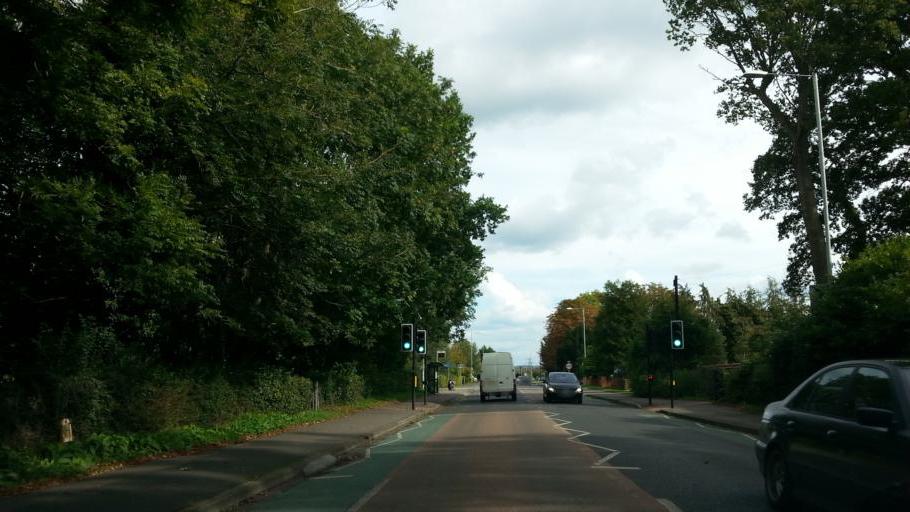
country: GB
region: England
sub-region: Wokingham
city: Earley
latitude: 51.4413
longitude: -0.9266
